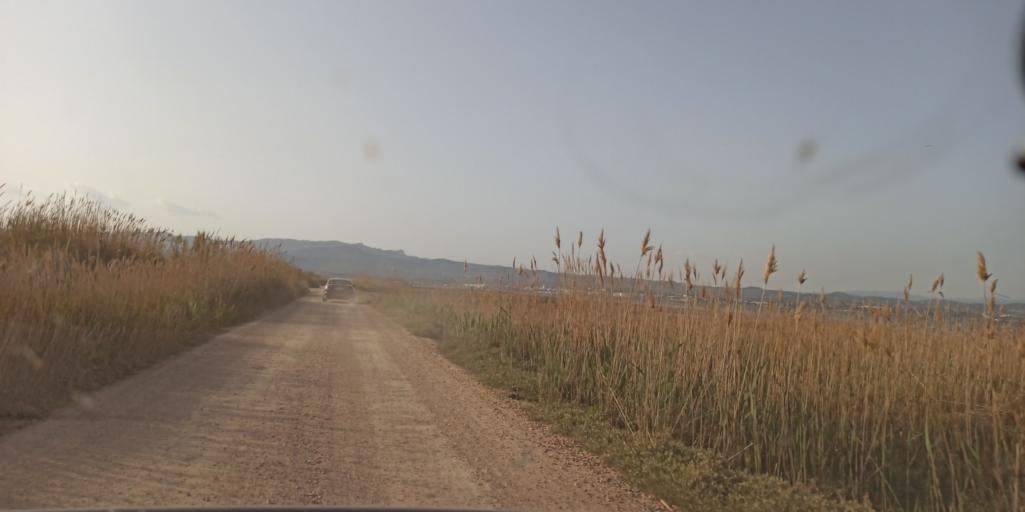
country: ES
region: Catalonia
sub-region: Provincia de Tarragona
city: L'Ampolla
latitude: 40.7746
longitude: 0.7250
